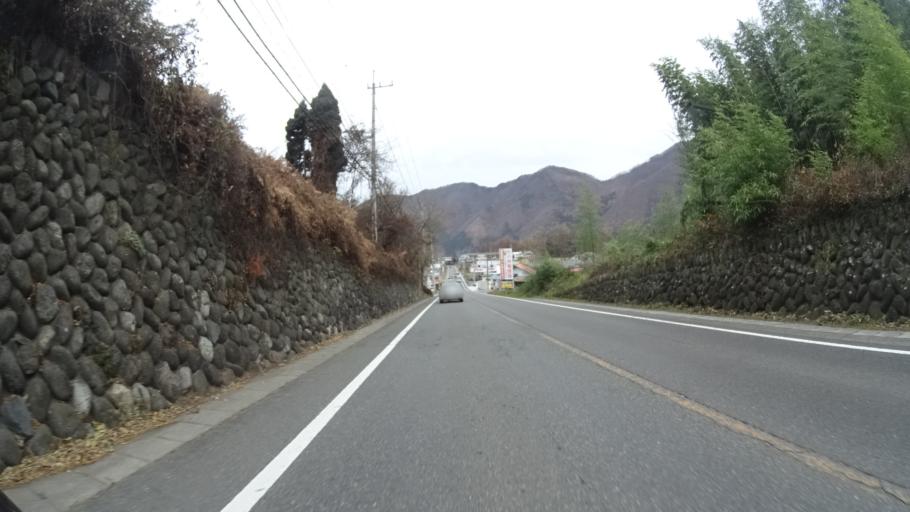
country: JP
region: Gunma
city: Numata
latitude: 36.6732
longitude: 139.1989
